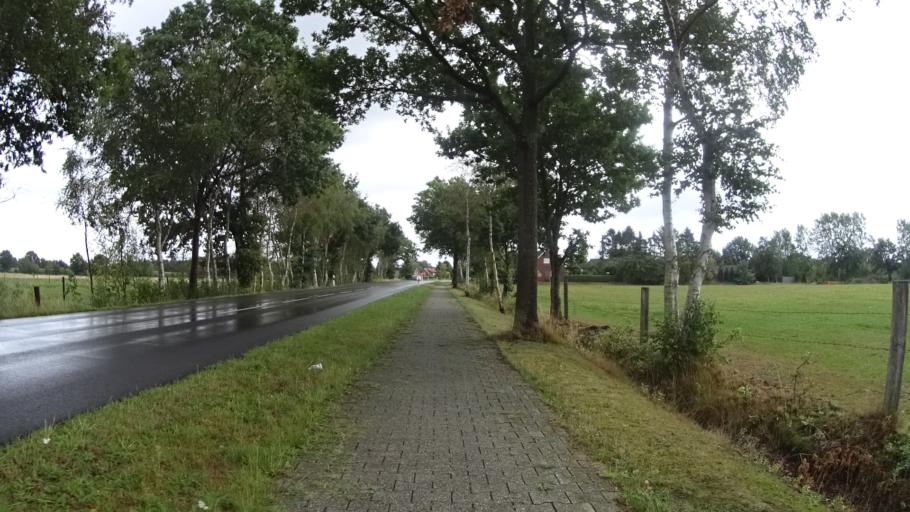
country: DE
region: Lower Saxony
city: Schwerinsdorf
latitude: 53.3454
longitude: 7.7405
